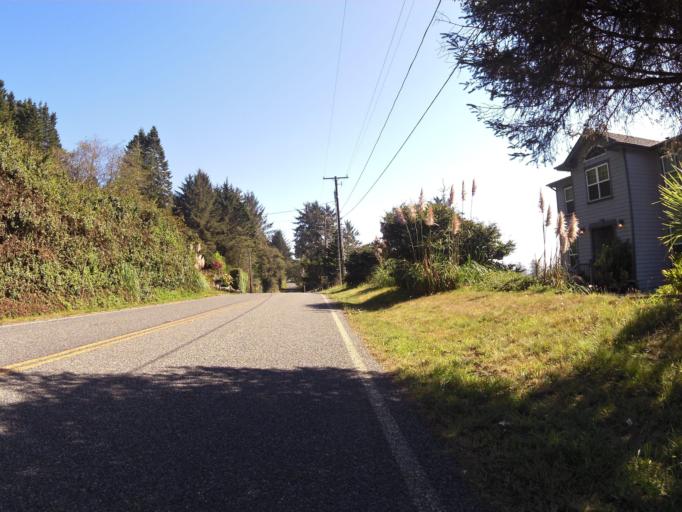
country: US
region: Oregon
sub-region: Curry County
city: Harbor
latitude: 41.9497
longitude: -124.1966
